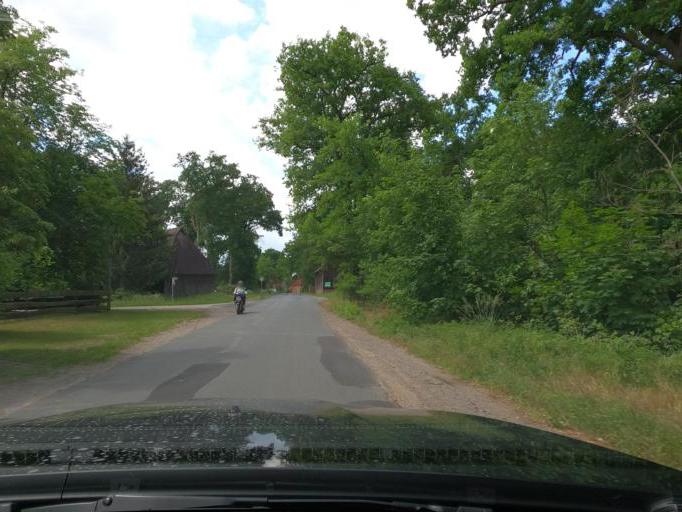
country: DE
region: Lower Saxony
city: Schwarmstedt
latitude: 52.6585
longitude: 9.6197
